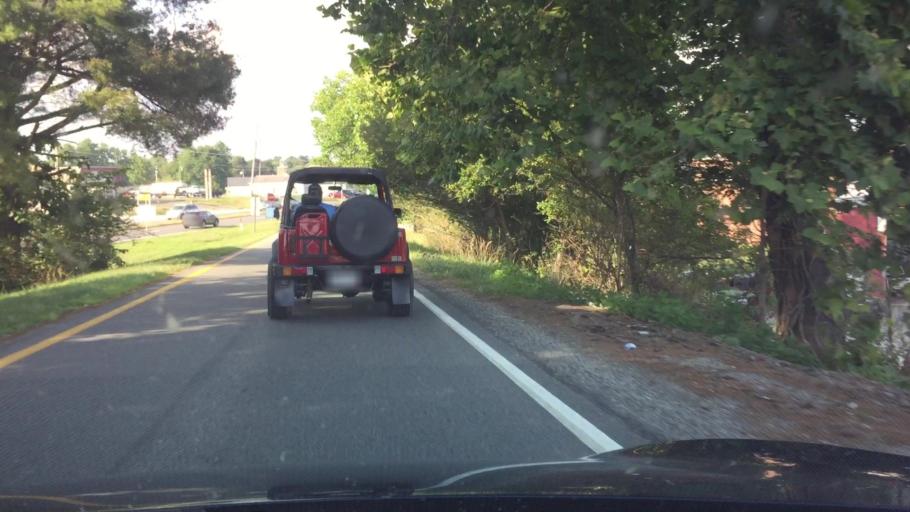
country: US
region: Virginia
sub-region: Pulaski County
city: Dublin
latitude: 37.1025
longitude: -80.6903
